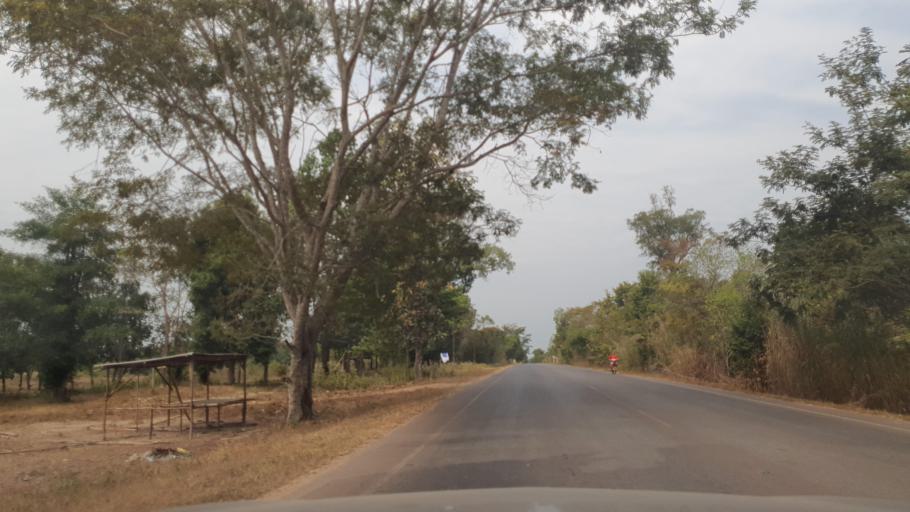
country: TH
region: Changwat Bueng Kan
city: Bung Khla
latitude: 18.2330
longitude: 104.0284
